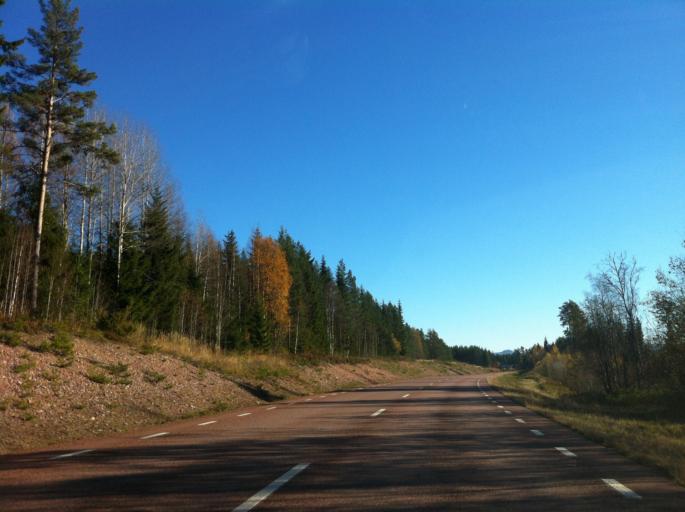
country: SE
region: Dalarna
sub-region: Alvdalens Kommun
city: AElvdalen
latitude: 61.2804
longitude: 13.9502
